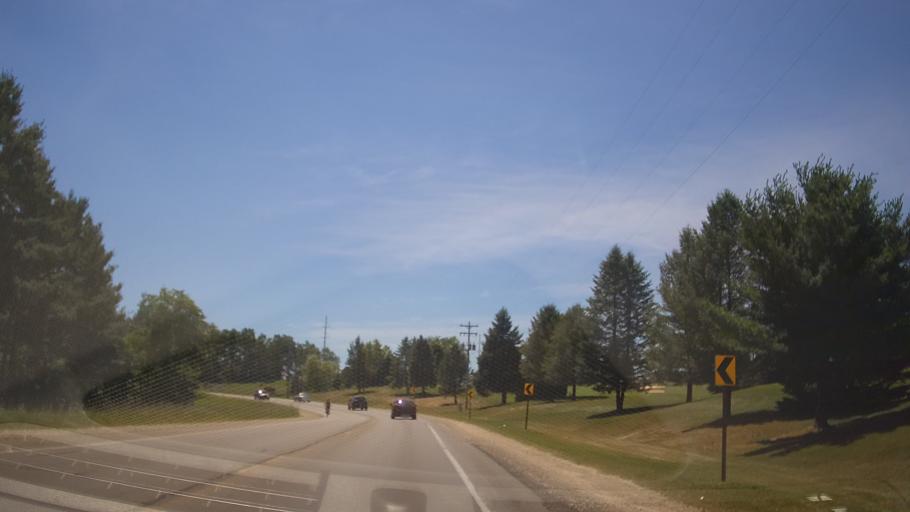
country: US
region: Michigan
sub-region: Grand Traverse County
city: Traverse City
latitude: 44.7217
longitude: -85.6825
